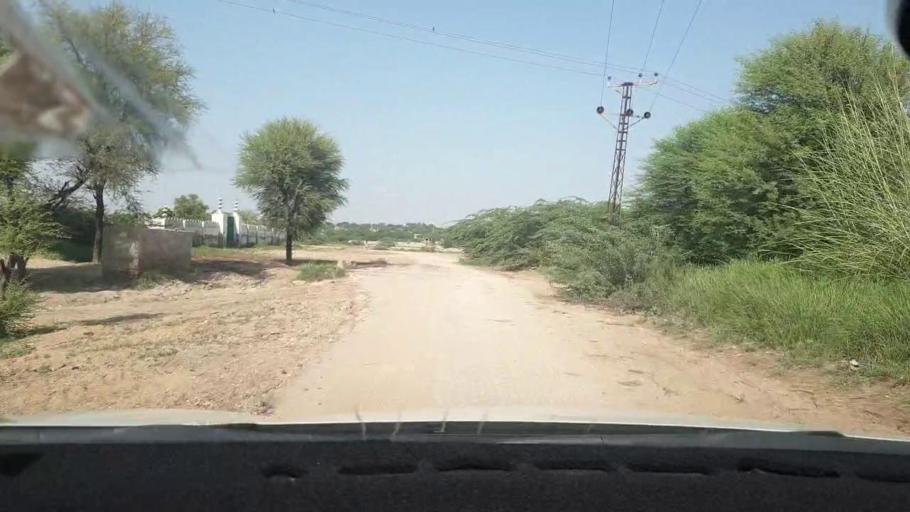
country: PK
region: Sindh
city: Tando Mittha Khan
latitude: 25.8589
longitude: 69.3861
